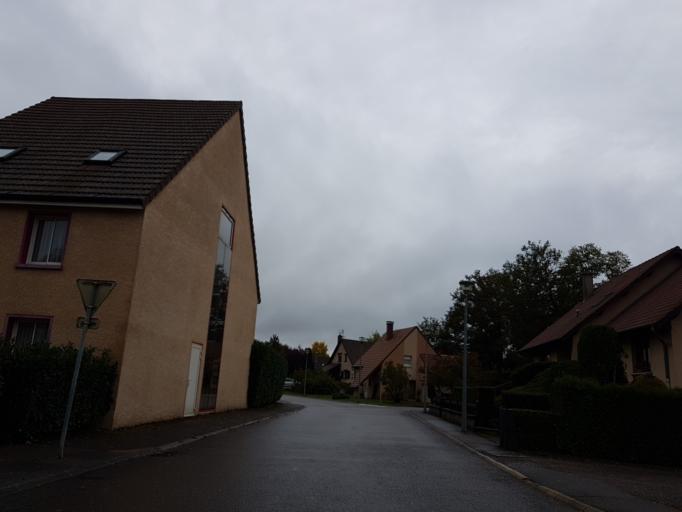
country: FR
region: Franche-Comte
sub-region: Departement de la Haute-Saone
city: Luxeuil-les-Bains
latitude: 47.8173
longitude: 6.3740
